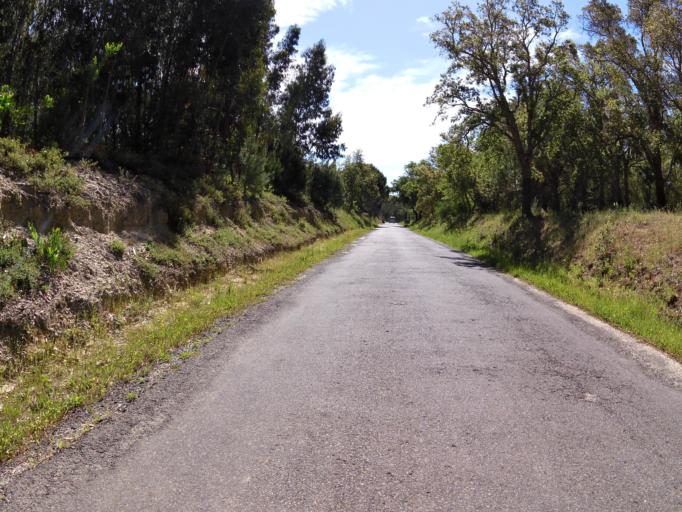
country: PT
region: Setubal
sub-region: Sines
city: Porto Covo
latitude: 37.9363
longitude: -8.7649
